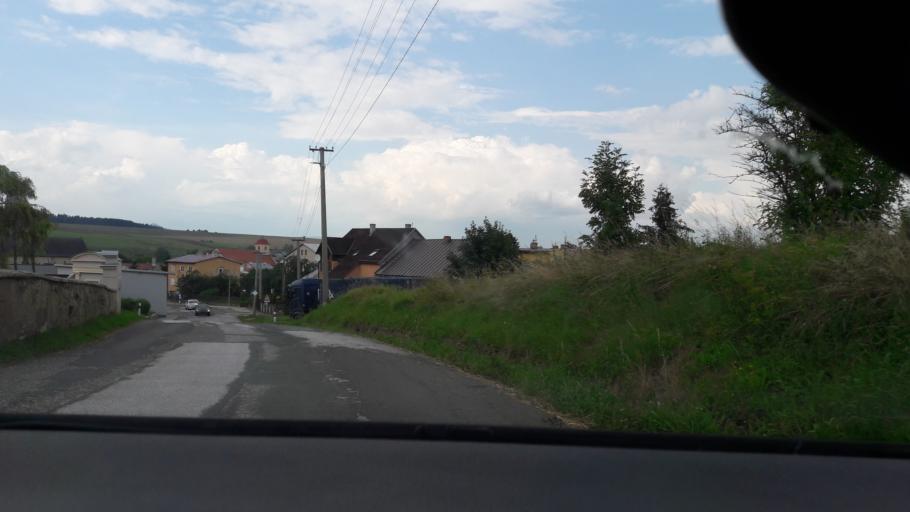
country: SK
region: Presovsky
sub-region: Okres Presov
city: Kezmarok
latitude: 49.1123
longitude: 20.3783
